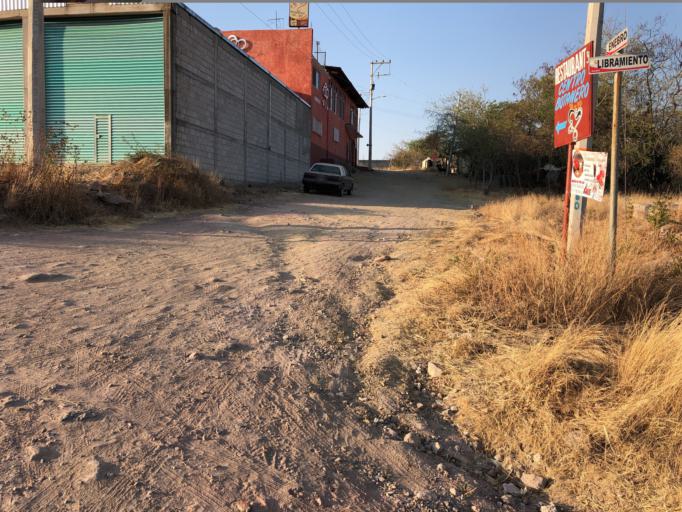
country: MX
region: Oaxaca
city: Ciudad de Huajuapam de Leon
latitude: 17.8345
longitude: -97.7882
